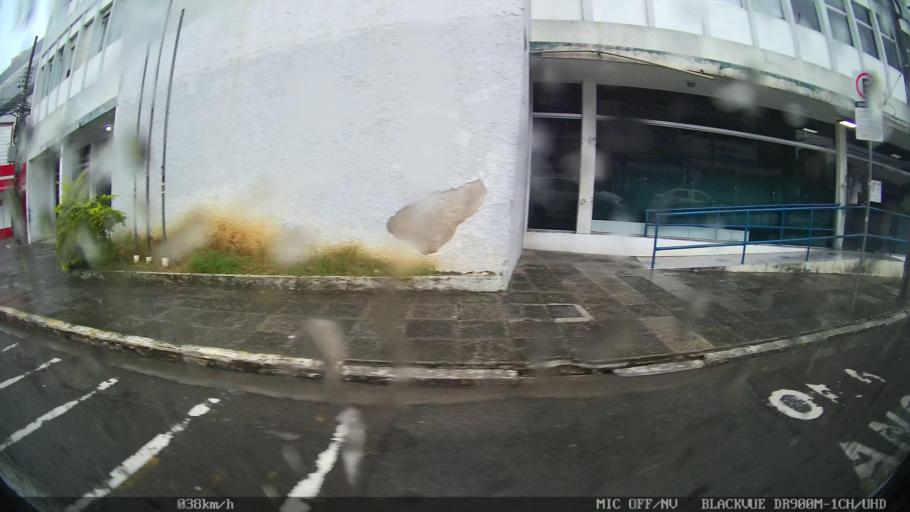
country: BR
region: Santa Catarina
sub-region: Itajai
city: Itajai
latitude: -26.9049
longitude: -48.6588
